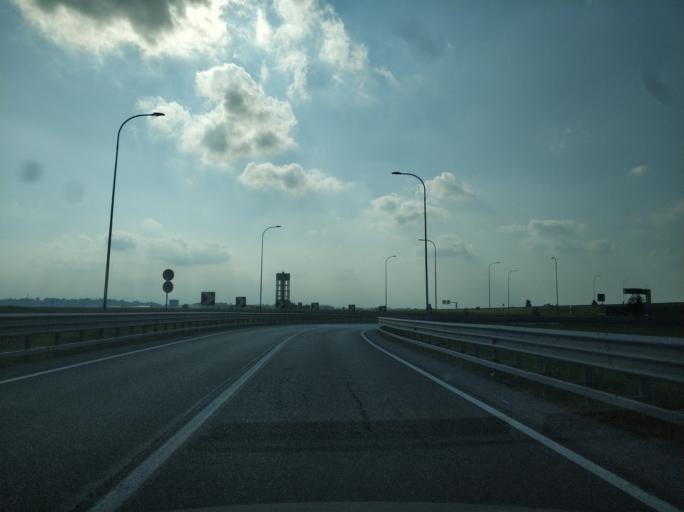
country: IT
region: Piedmont
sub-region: Provincia di Cuneo
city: Roreto
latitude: 44.6631
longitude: 7.8037
